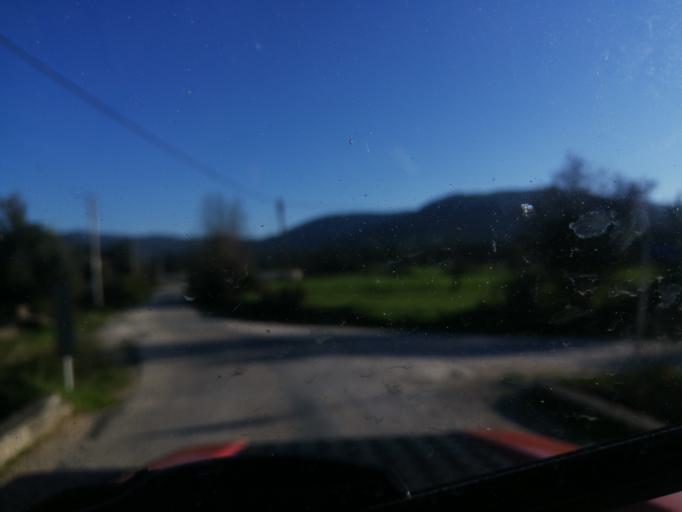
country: TR
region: Antalya
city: Kas
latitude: 36.2870
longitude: 29.7058
